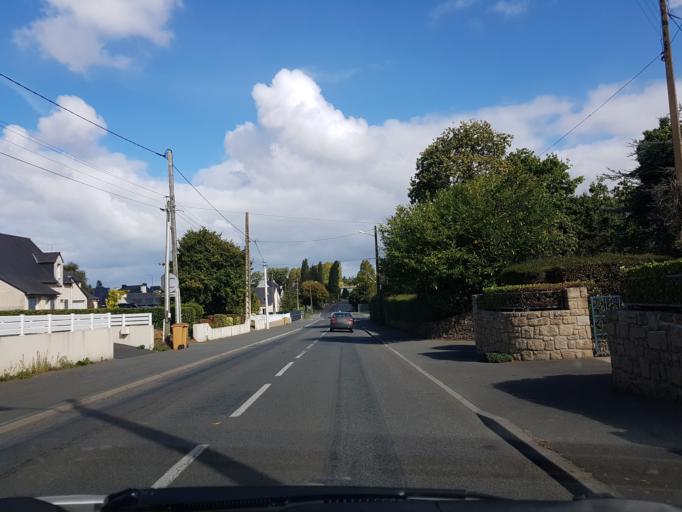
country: FR
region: Brittany
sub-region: Departement des Cotes-d'Armor
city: Pledran
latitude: 48.4705
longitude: -2.7616
